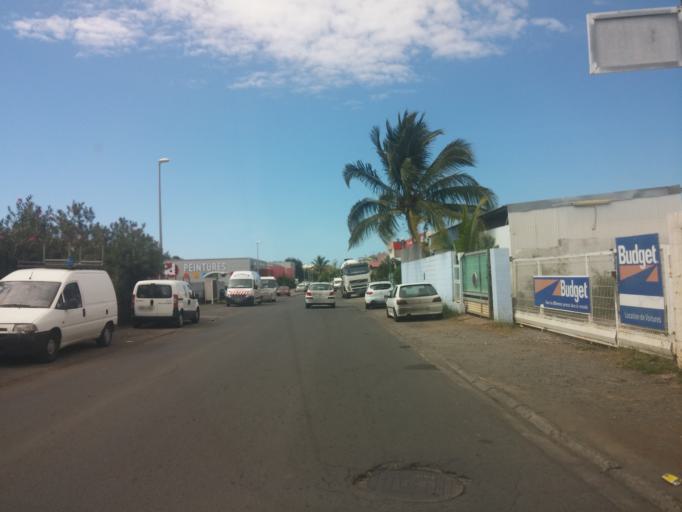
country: RE
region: Reunion
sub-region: Reunion
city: Sainte-Marie
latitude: -20.8988
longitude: 55.5325
